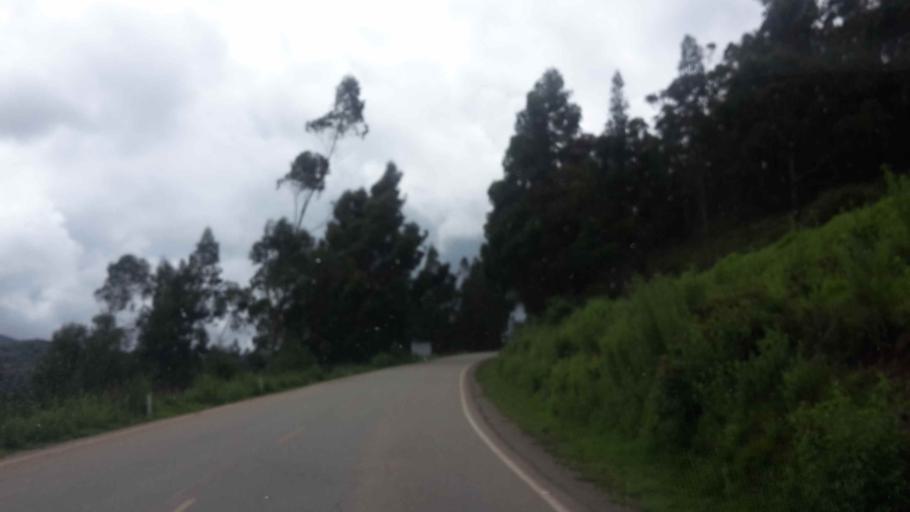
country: BO
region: Cochabamba
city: Totora
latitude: -17.5577
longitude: -65.3426
